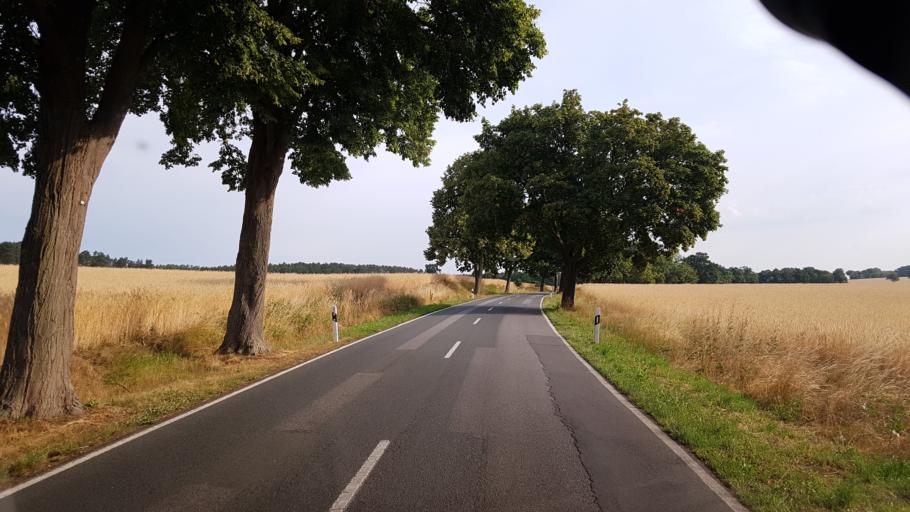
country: DE
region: Brandenburg
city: Golssen
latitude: 51.9605
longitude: 13.5429
